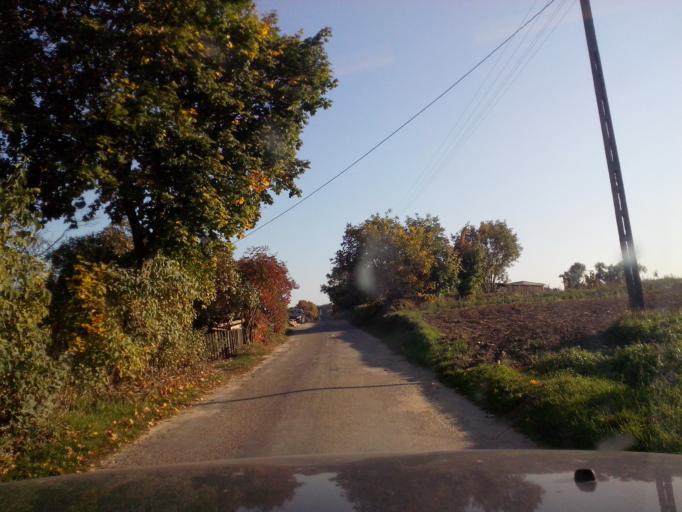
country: PL
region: Kujawsko-Pomorskie
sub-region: Powiat brodnicki
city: Bartniczka
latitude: 53.2838
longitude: 19.6973
